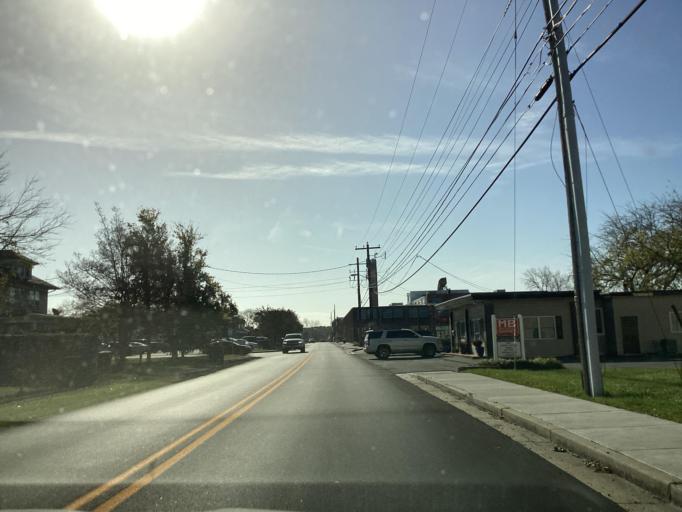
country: US
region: Maryland
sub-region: Dorchester County
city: Cambridge
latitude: 38.5636
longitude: -76.0677
